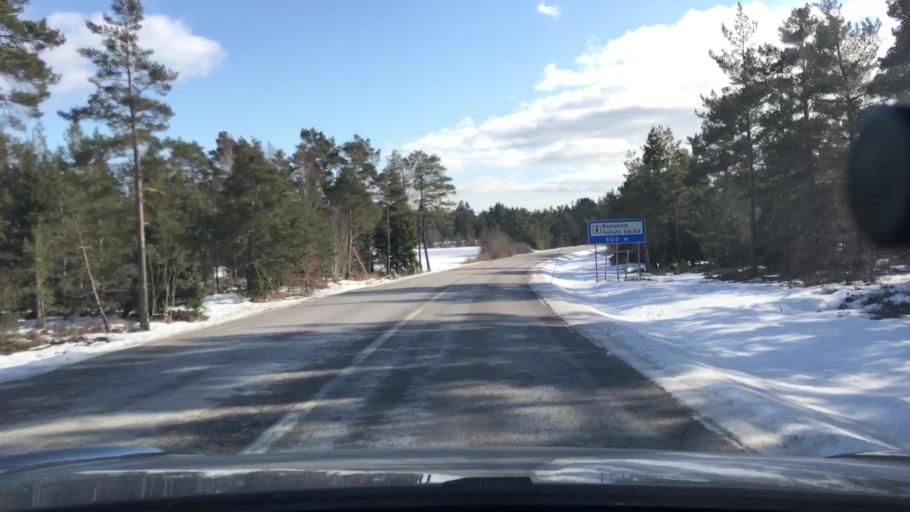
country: SE
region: Gotland
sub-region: Gotland
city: Hemse
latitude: 57.3458
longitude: 18.6928
